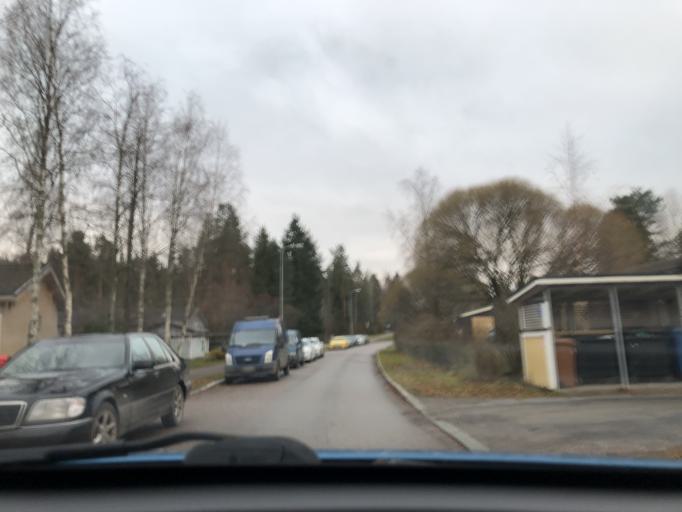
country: FI
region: Pirkanmaa
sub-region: Tampere
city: Kangasala
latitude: 61.5264
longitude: 23.9520
